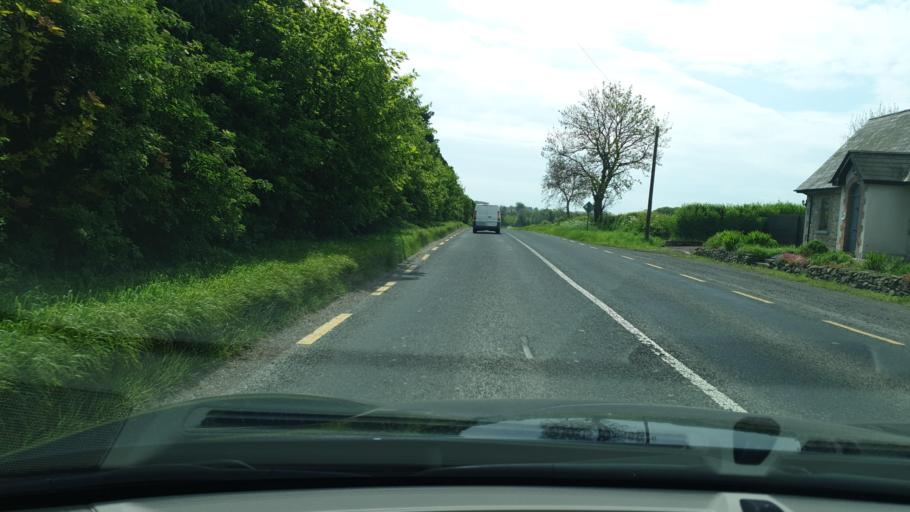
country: IE
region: Ulster
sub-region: An Cabhan
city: Kingscourt
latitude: 53.7912
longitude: -6.7368
